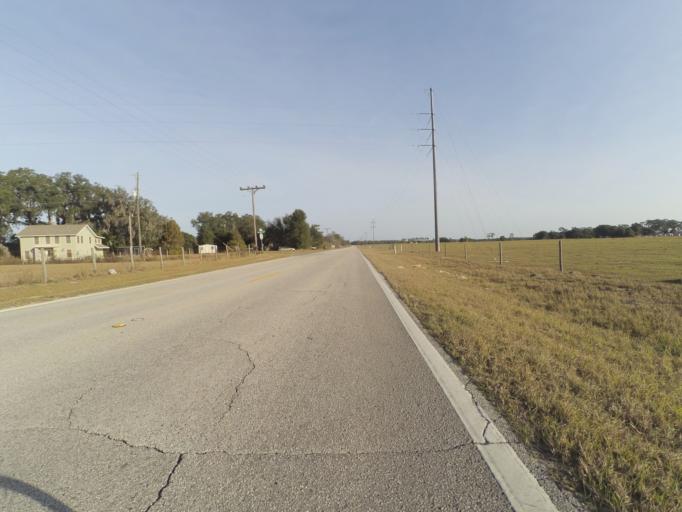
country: US
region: Florida
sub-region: Lake County
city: Umatilla
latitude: 28.9526
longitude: -81.6304
